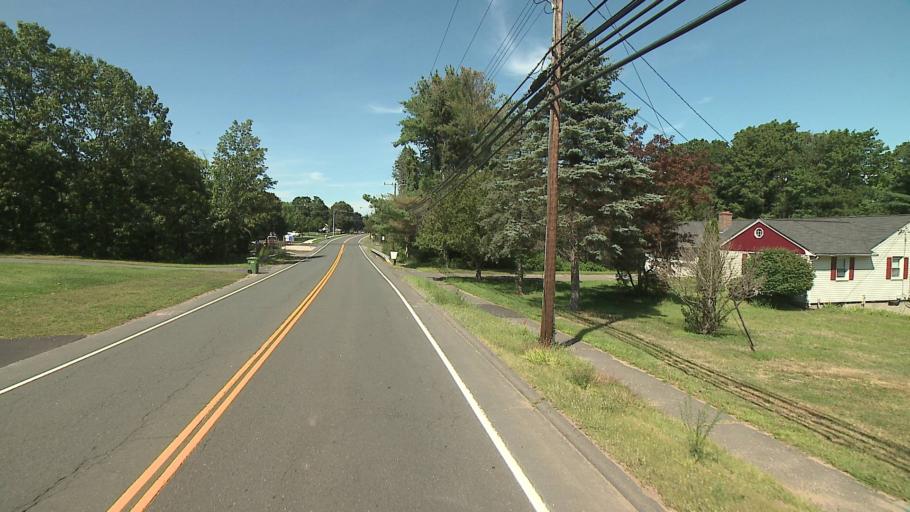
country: US
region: Connecticut
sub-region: Hartford County
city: Canton Valley
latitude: 41.7870
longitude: -72.8637
